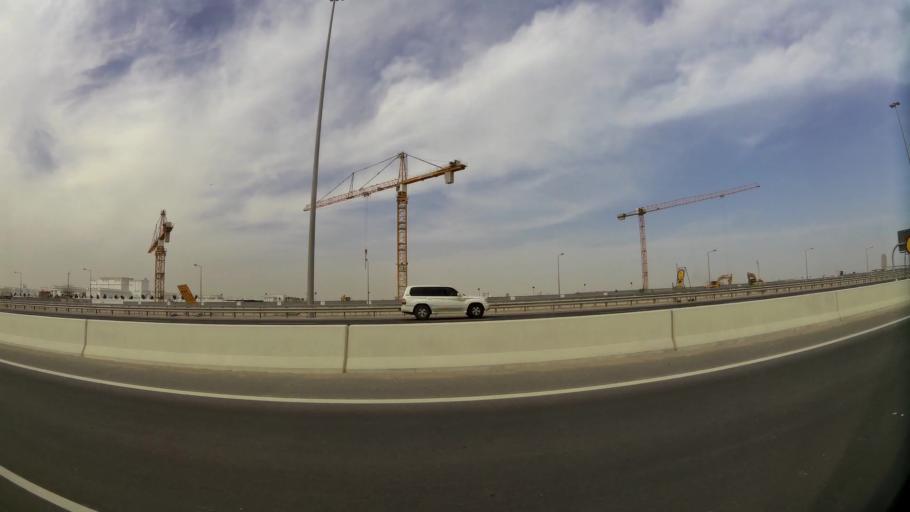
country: QA
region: Baladiyat ar Rayyan
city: Ar Rayyan
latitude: 25.3169
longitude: 51.3615
